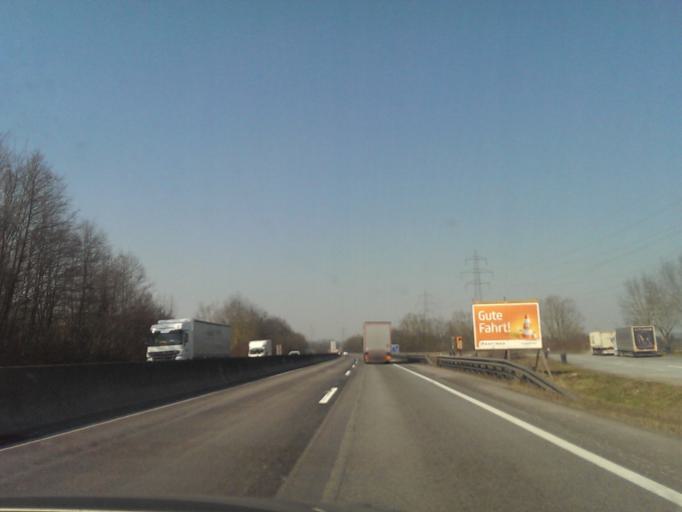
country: AT
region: Upper Austria
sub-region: Politischer Bezirk Vocklabruck
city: Wolfsegg am Hausruck
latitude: 48.2077
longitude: 13.6342
